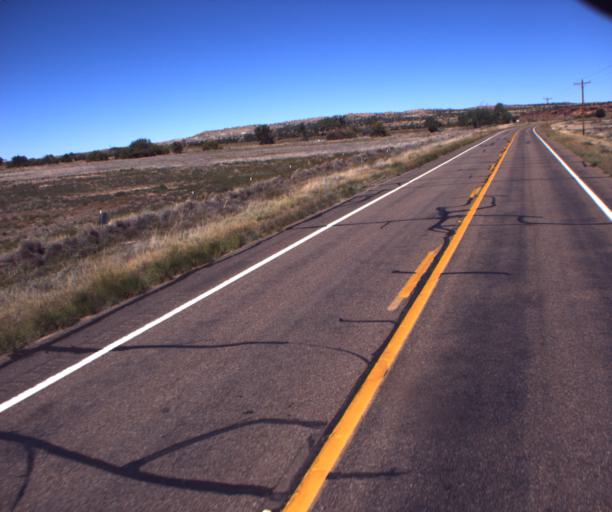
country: US
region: Arizona
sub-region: Apache County
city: Saint Johns
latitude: 34.4428
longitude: -109.4106
